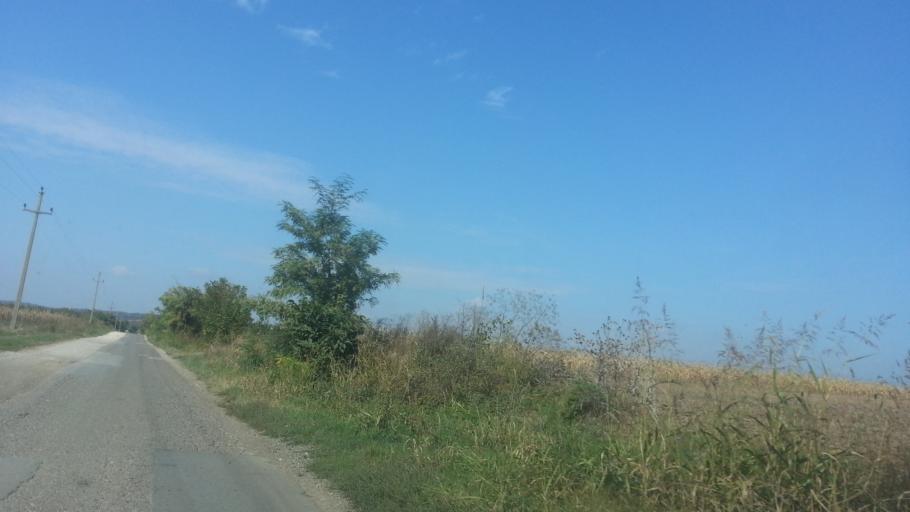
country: RS
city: Novi Slankamen
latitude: 45.1237
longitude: 20.2633
